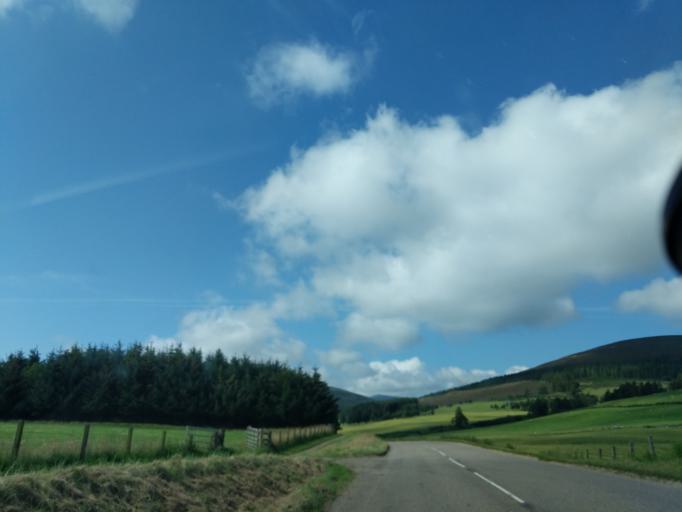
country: GB
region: Scotland
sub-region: Moray
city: Dufftown
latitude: 57.4419
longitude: -3.1427
